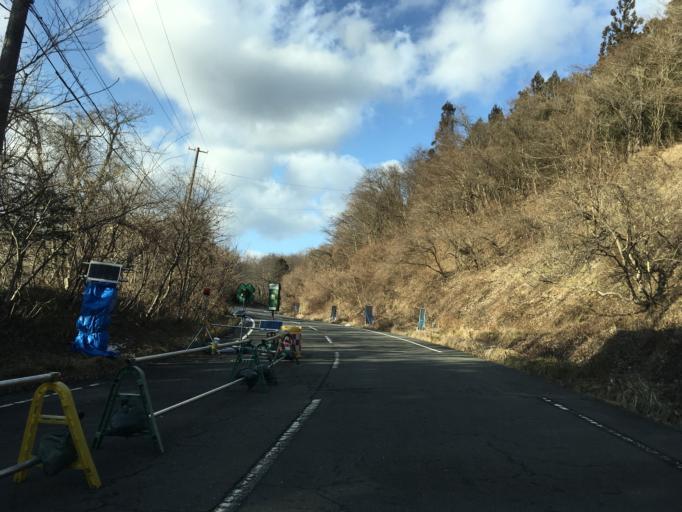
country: JP
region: Miyagi
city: Furukawa
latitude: 38.8079
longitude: 140.8260
